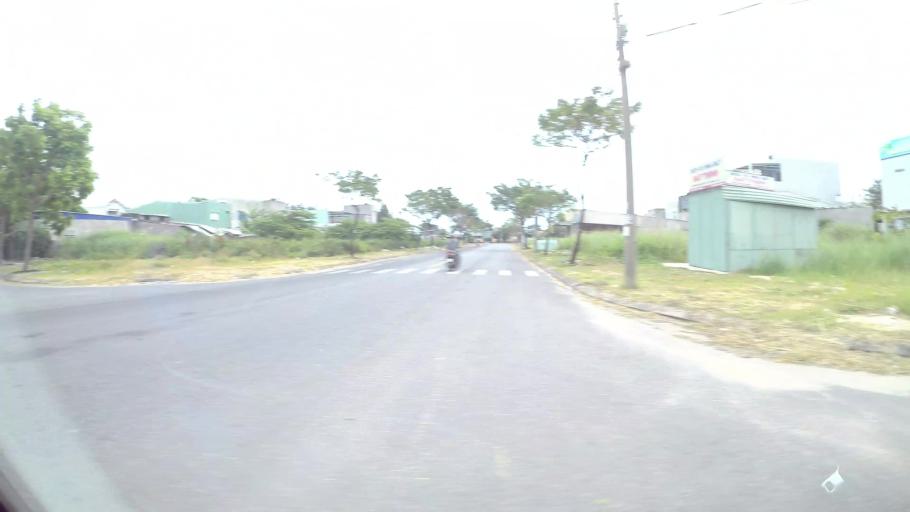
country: VN
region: Da Nang
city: Da Nang
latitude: 16.0986
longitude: 108.2328
